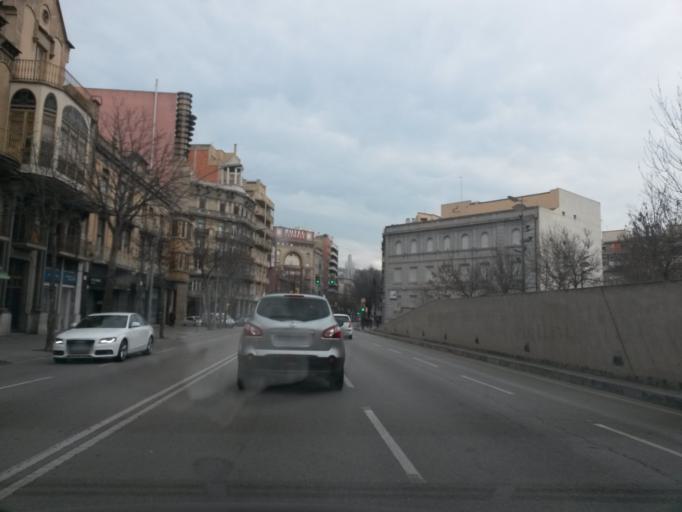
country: ES
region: Catalonia
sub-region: Provincia de Girona
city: Girona
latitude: 41.9839
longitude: 2.8201
